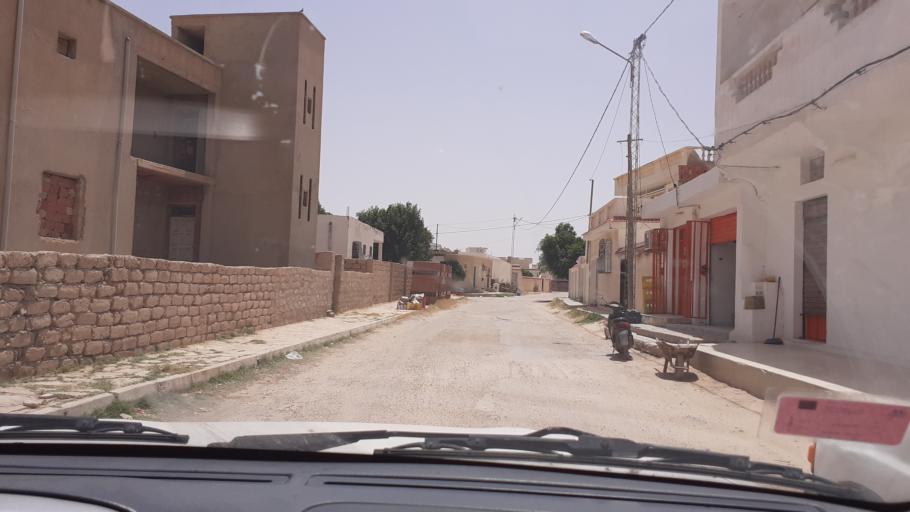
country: TN
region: Qabis
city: Matmata
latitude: 33.6138
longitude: 10.2867
